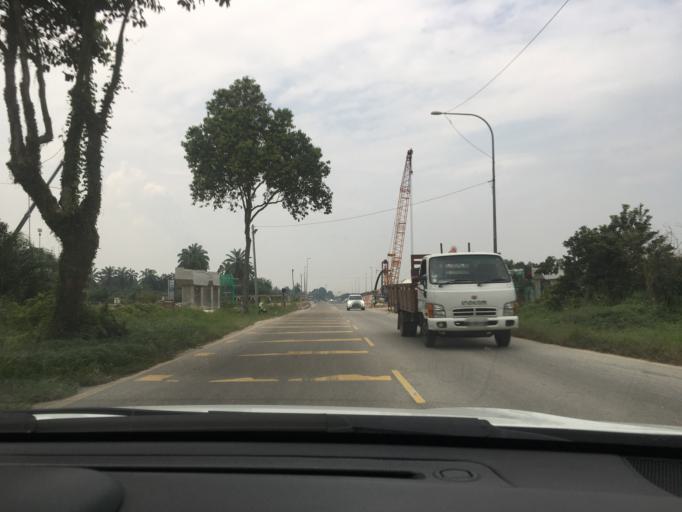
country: MY
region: Selangor
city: Klang
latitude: 3.1362
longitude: 101.4015
